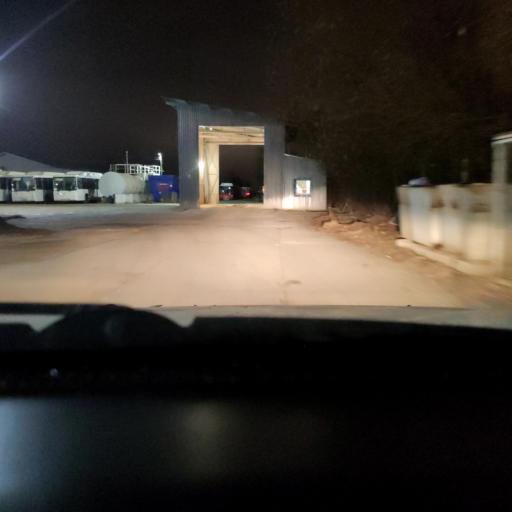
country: RU
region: Perm
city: Kondratovo
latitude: 57.9514
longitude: 56.0885
